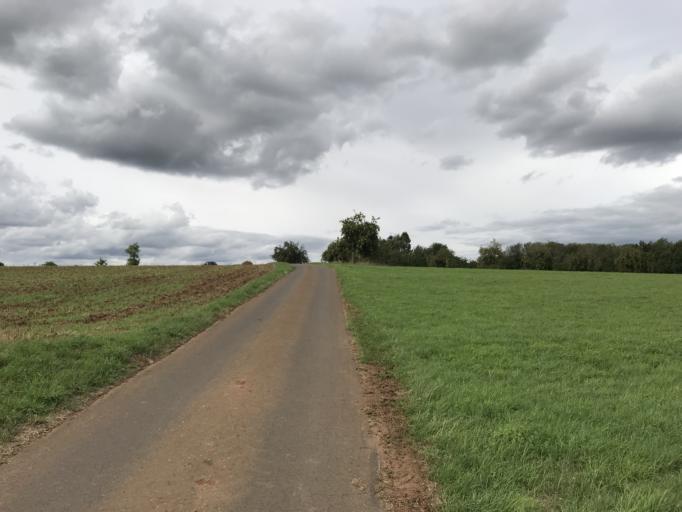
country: DE
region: Hesse
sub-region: Regierungsbezirk Giessen
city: Grunberg
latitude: 50.5528
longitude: 8.9310
